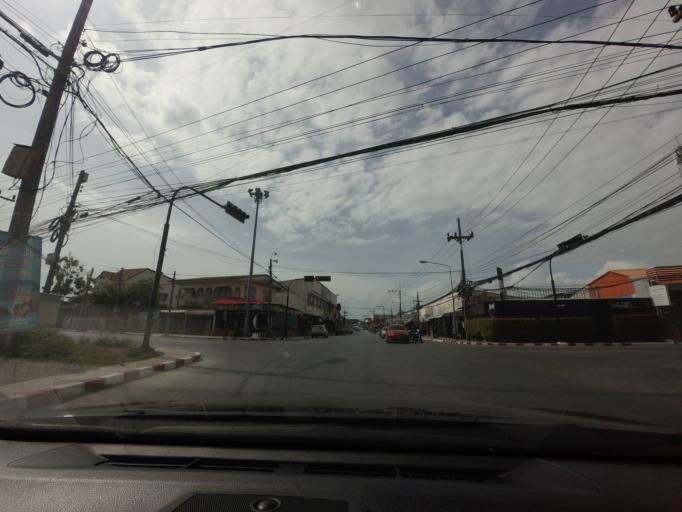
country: TH
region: Pattani
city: Pattani
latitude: 6.8731
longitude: 101.2493
